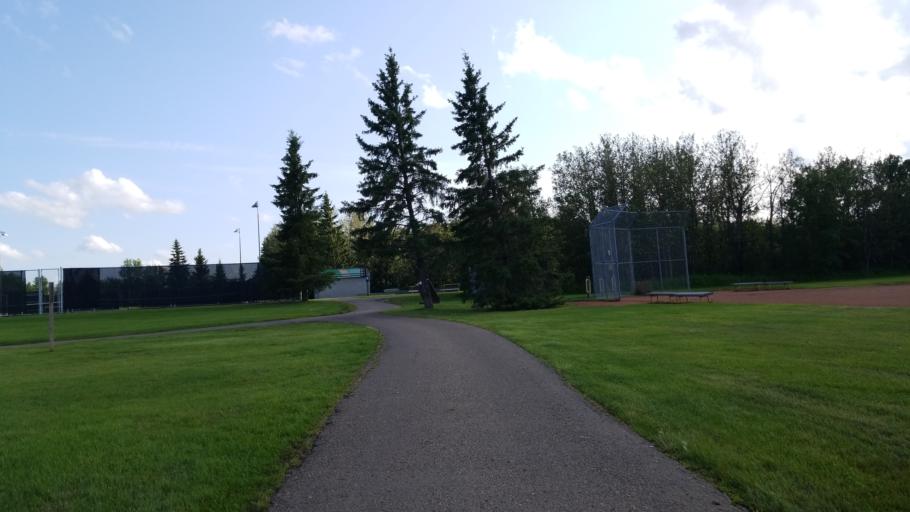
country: CA
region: Saskatchewan
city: Lloydminster
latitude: 53.2639
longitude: -110.0368
